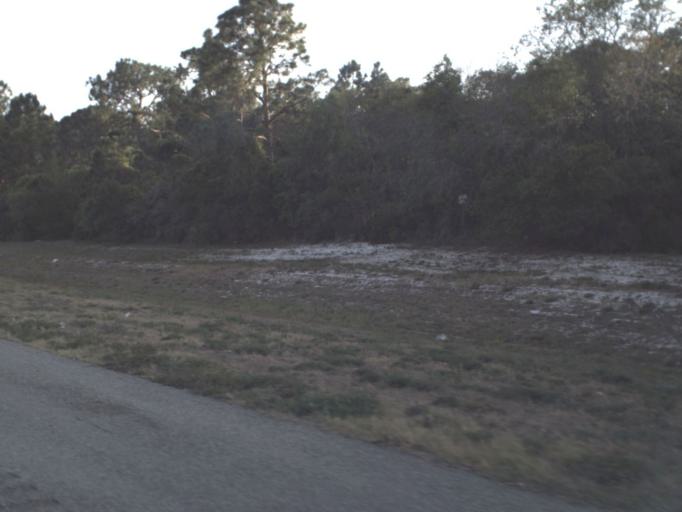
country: US
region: Florida
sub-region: Brevard County
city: Port Saint John
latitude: 28.4785
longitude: -80.8216
